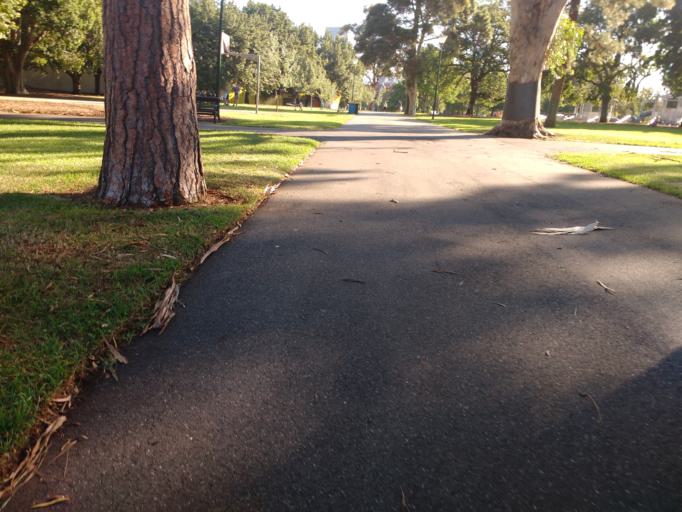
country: AU
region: Victoria
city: Carlton
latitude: -37.8019
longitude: 144.9715
